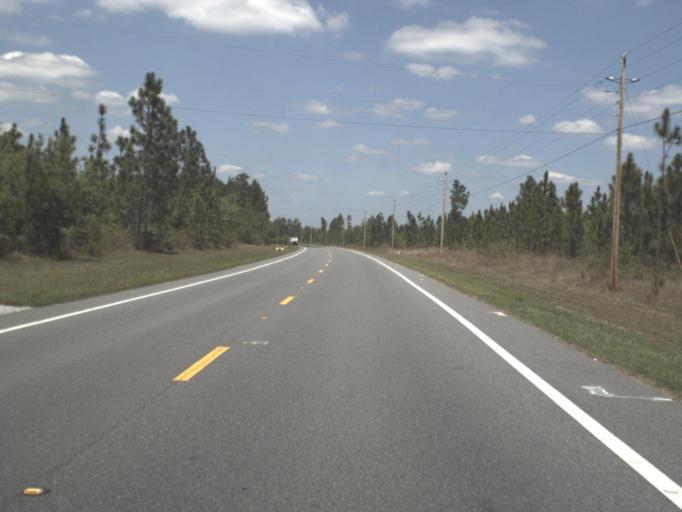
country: US
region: Alabama
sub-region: Escambia County
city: East Brewton
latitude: 30.9227
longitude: -87.0232
